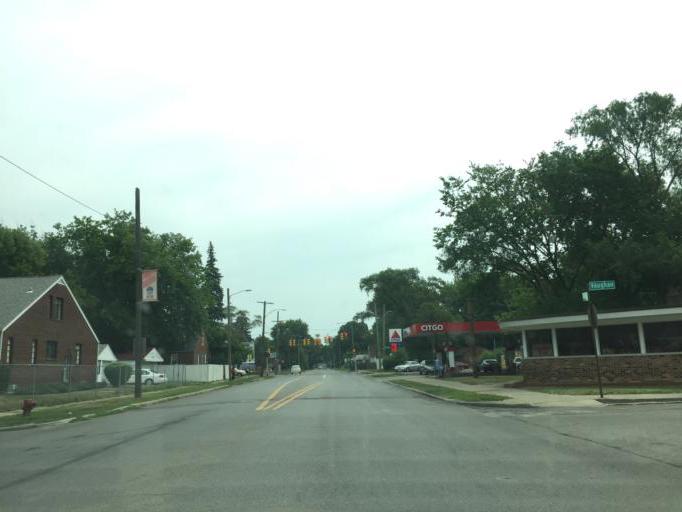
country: US
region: Michigan
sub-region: Wayne County
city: Redford
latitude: 42.4006
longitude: -83.2387
